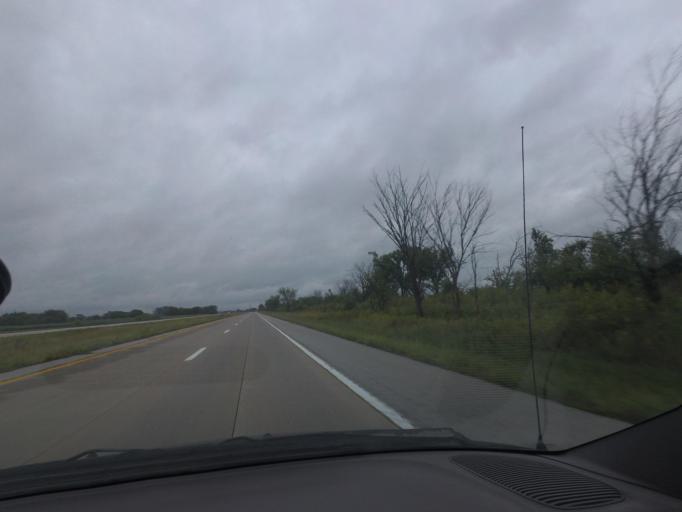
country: US
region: Missouri
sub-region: Marion County
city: Monroe City
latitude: 39.6605
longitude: -91.8211
